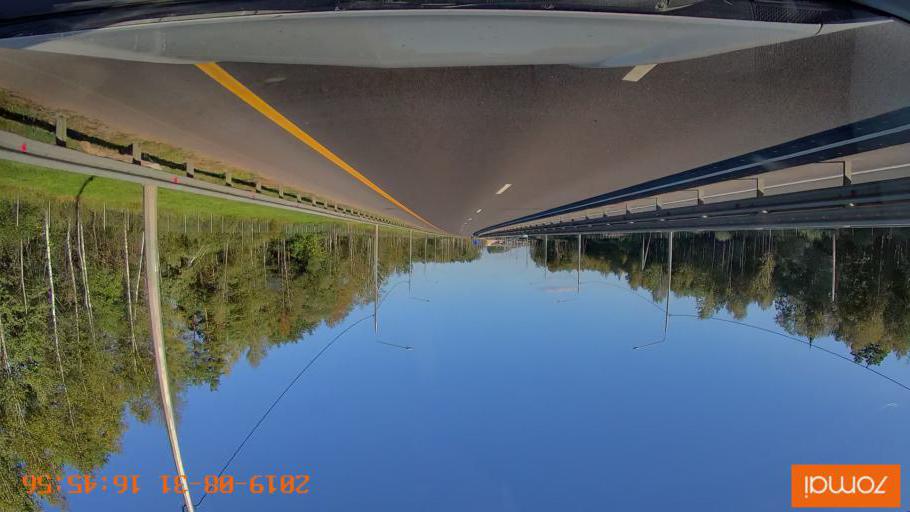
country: RU
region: Kaluga
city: Mstikhino
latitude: 54.6271
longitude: 36.1260
